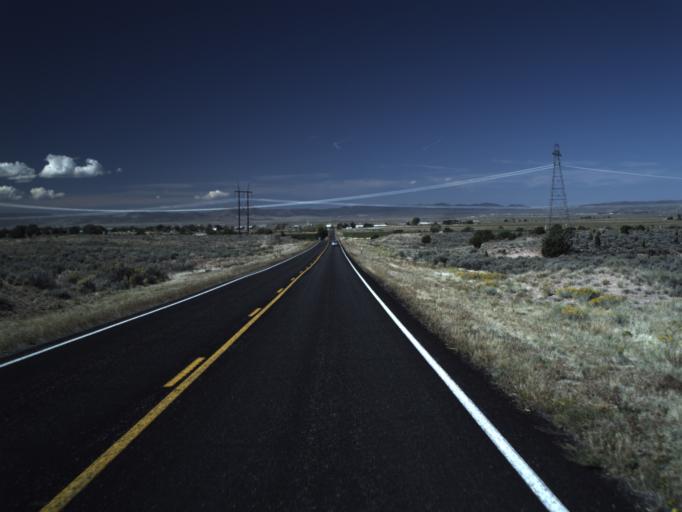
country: US
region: Utah
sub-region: Washington County
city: Enterprise
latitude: 37.6747
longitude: -113.5239
